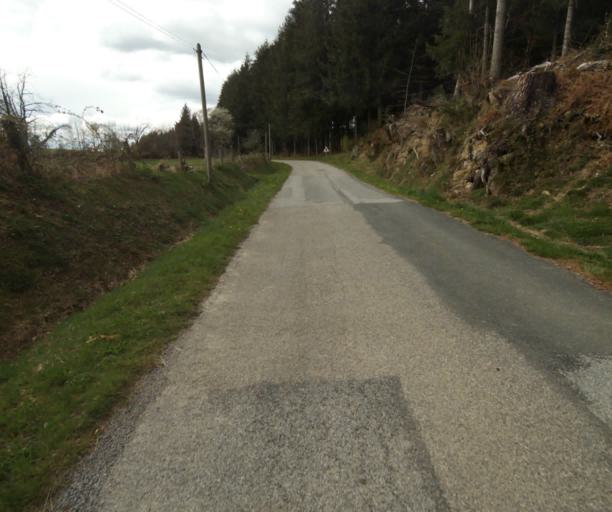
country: FR
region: Limousin
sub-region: Departement de la Correze
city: Argentat
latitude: 45.1884
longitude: 1.9337
